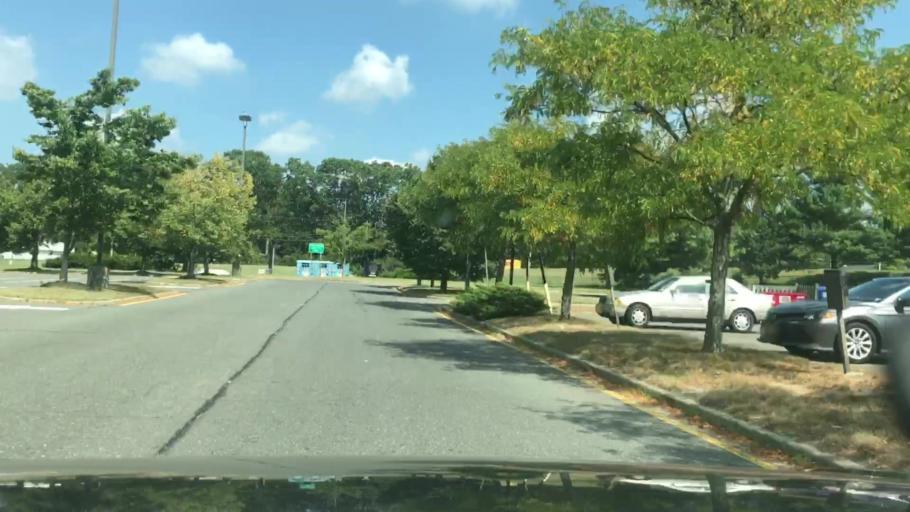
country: US
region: New Jersey
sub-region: Ocean County
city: Silver Ridge
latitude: 39.9915
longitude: -74.2131
